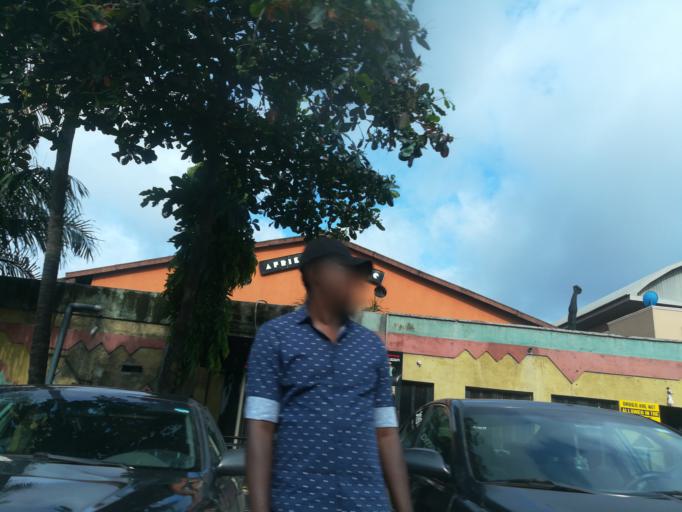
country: NG
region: Lagos
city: Ikeja
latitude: 6.6228
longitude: 3.3564
